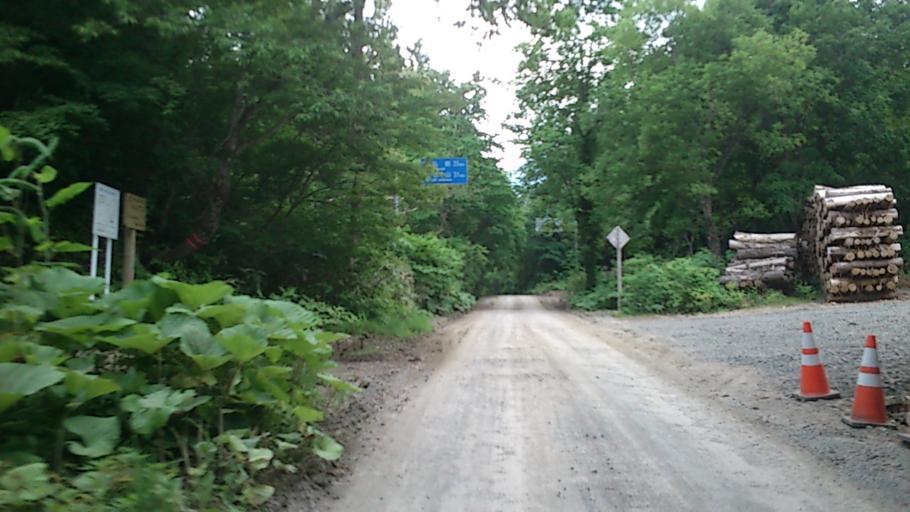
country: JP
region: Aomori
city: Hirosaki
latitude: 40.5339
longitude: 140.1838
